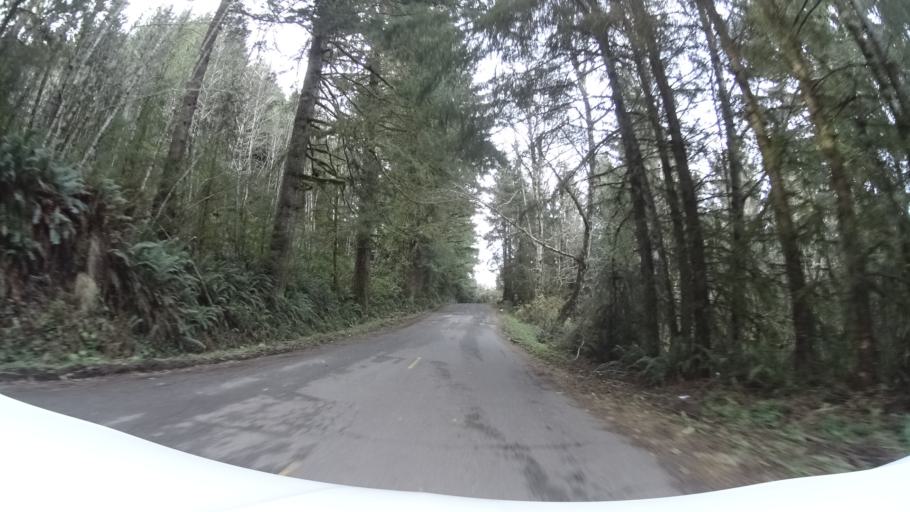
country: US
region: California
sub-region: Humboldt County
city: Ferndale
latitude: 40.5393
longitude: -124.2773
